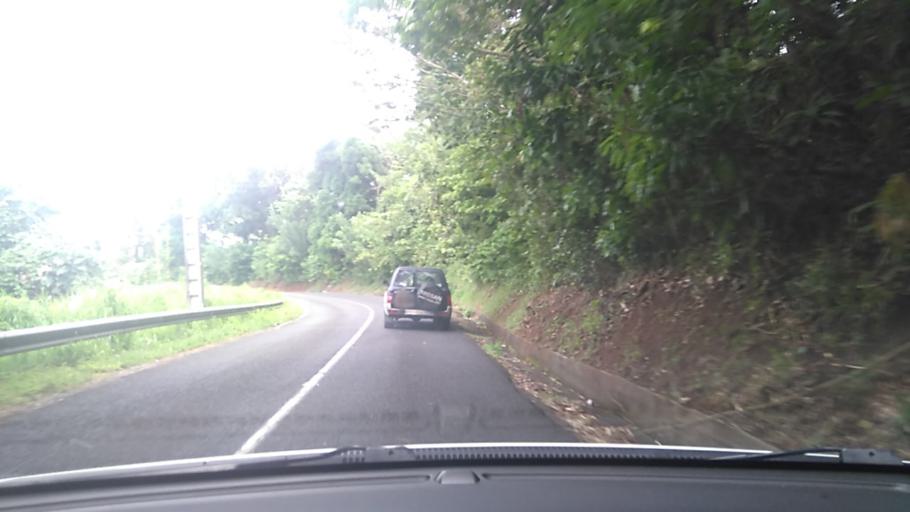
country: MQ
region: Martinique
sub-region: Martinique
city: Saint-Esprit
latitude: 14.5579
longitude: -60.9192
